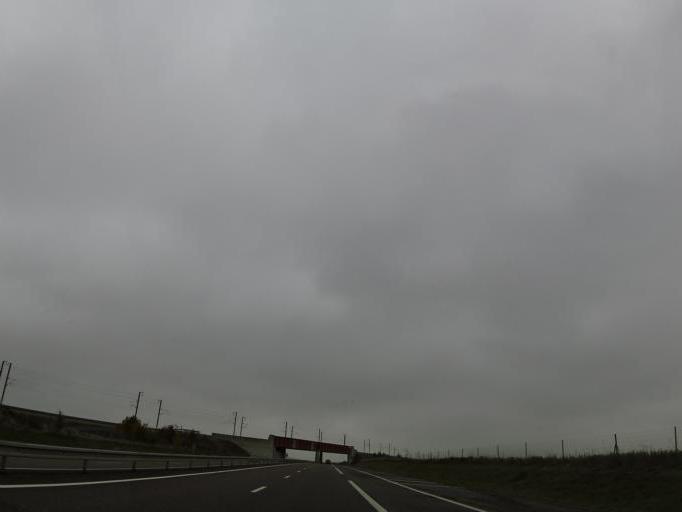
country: FR
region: Champagne-Ardenne
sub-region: Departement de la Marne
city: Courtisols
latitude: 49.0310
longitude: 4.5510
